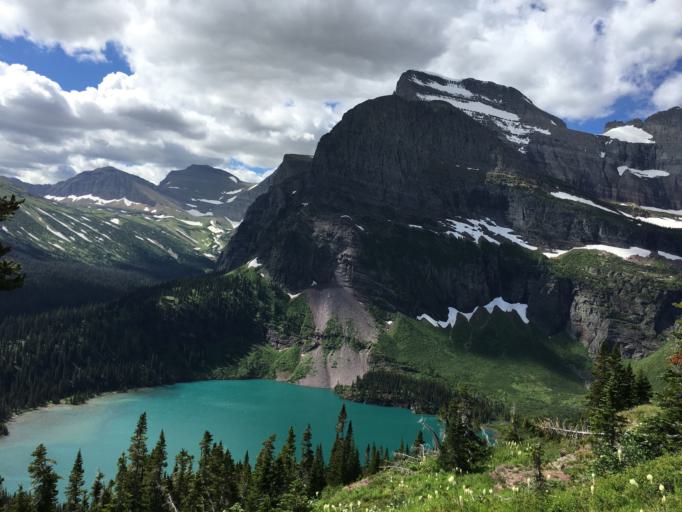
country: CA
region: Alberta
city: Cardston
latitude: 48.7738
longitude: -113.7061
